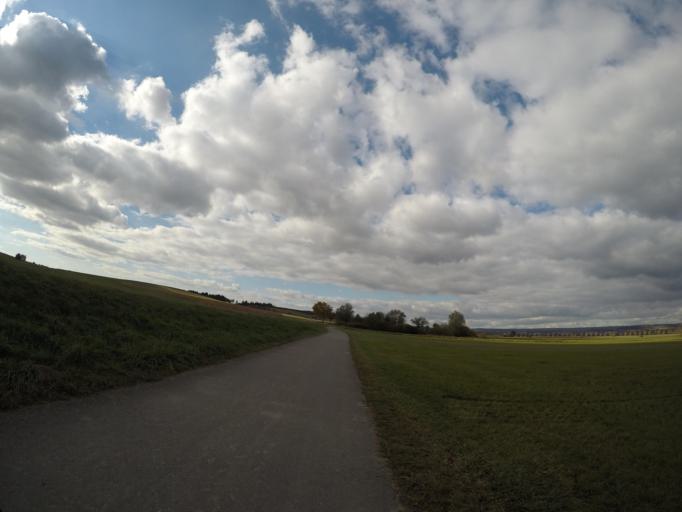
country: DE
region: Baden-Wuerttemberg
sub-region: Tuebingen Region
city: Unterstadion
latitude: 48.2076
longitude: 9.6784
